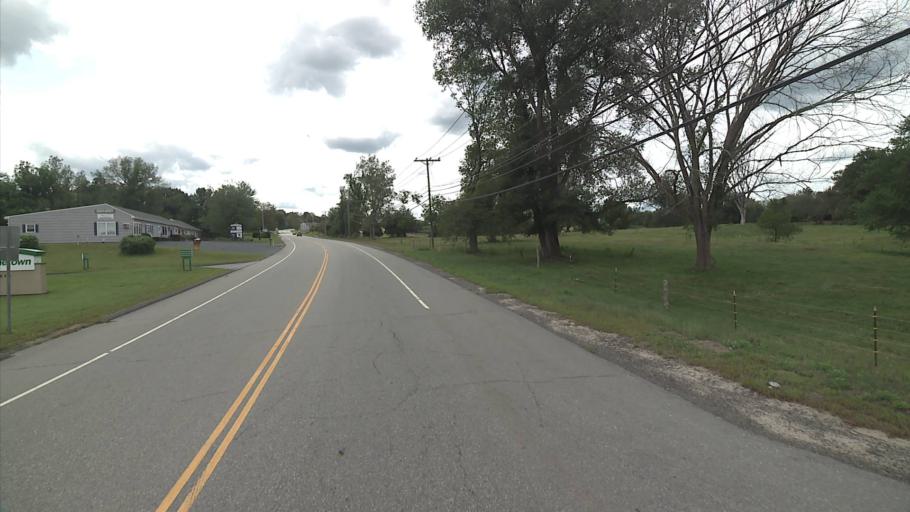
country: US
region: Connecticut
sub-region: Windham County
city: South Woodstock
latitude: 41.9343
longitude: -71.9463
